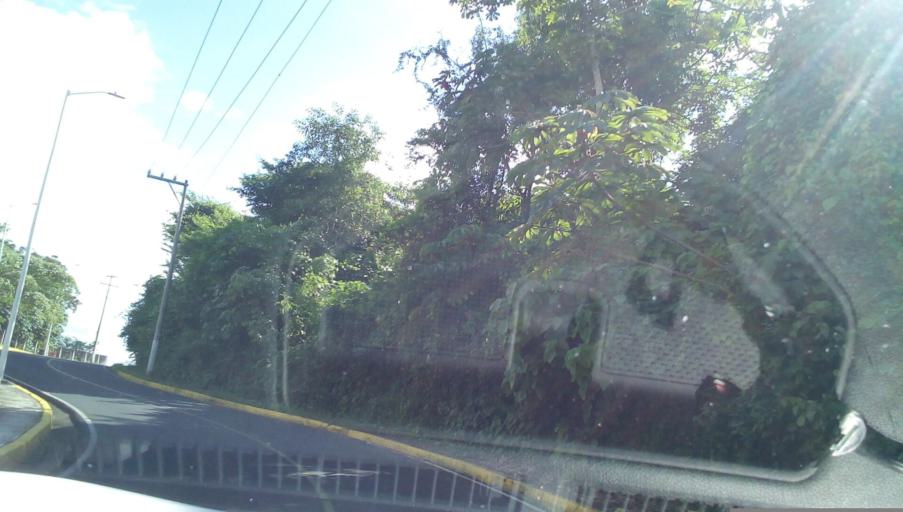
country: MX
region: Veracruz
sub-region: Cordoba
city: El Porvenir
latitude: 18.9035
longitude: -96.9228
